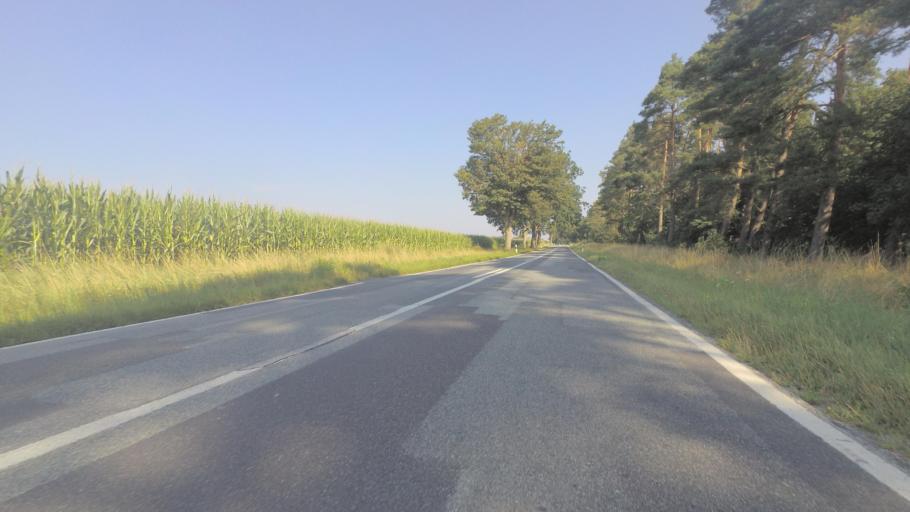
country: DE
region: Mecklenburg-Vorpommern
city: Grabowhofe
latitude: 53.6031
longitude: 12.4692
